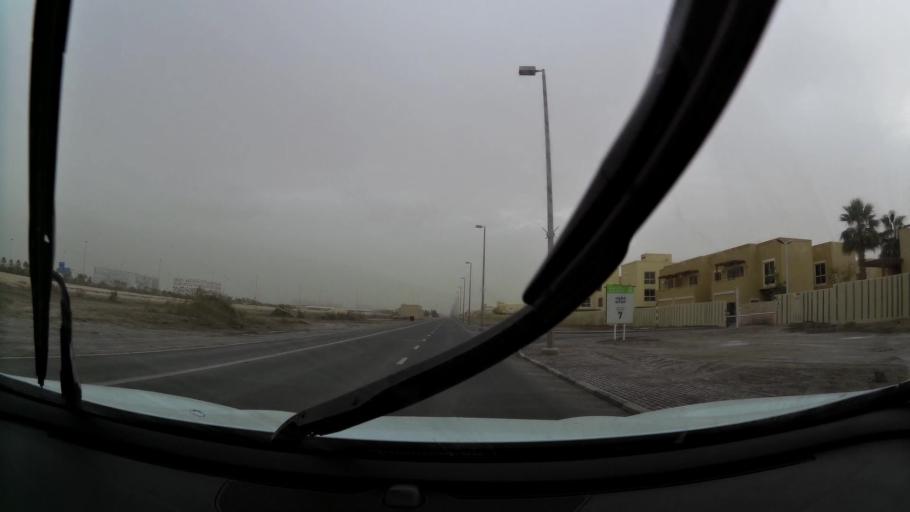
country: AE
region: Abu Dhabi
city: Abu Dhabi
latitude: 24.4367
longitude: 54.5786
